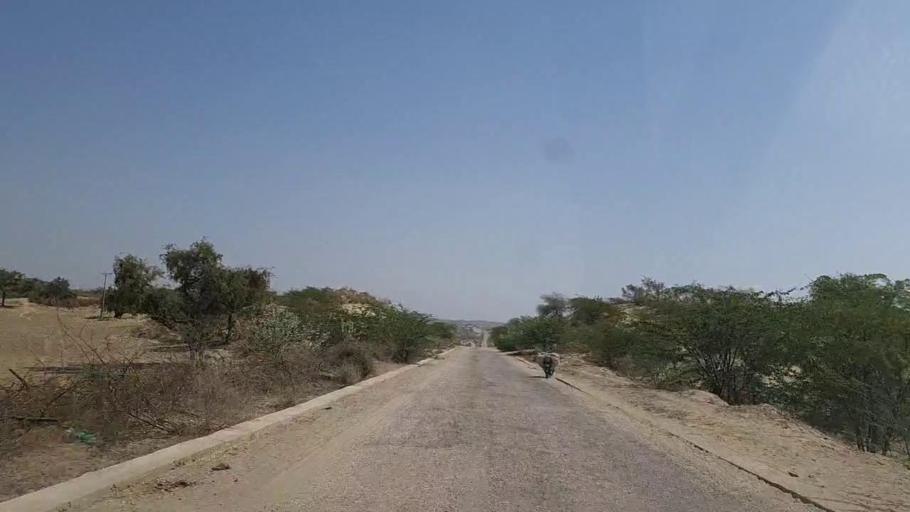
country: PK
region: Sindh
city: Diplo
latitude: 24.5137
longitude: 69.3911
